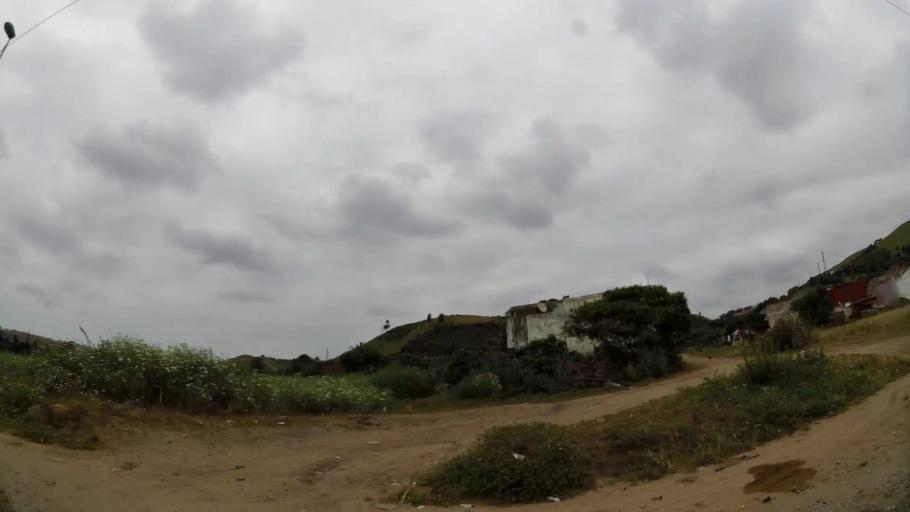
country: MA
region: Rabat-Sale-Zemmour-Zaer
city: Sale
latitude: 33.9916
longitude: -6.7654
